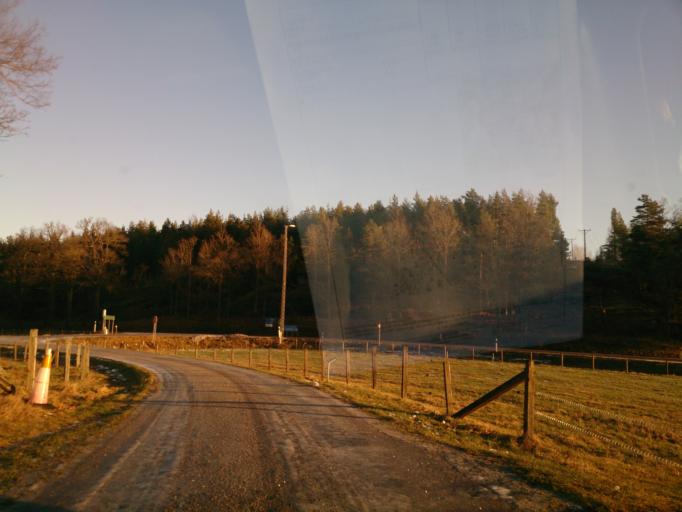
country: SE
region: OEstergoetland
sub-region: Atvidabergs Kommun
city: Atvidaberg
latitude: 58.2927
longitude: 15.8928
